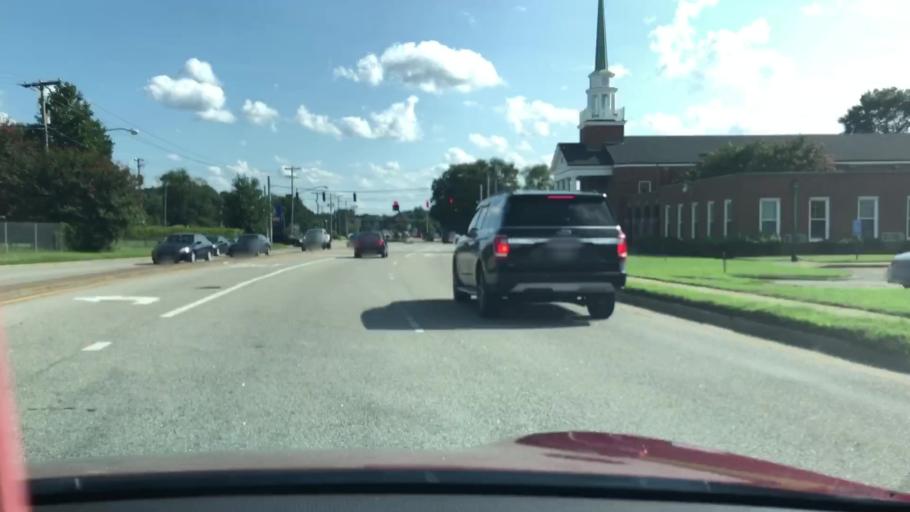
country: US
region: Virginia
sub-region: City of Virginia Beach
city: Virginia Beach
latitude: 36.8451
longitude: -76.0208
